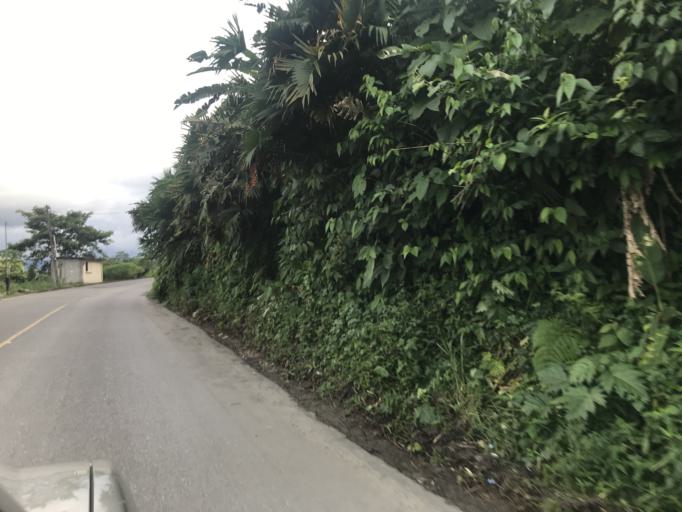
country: EC
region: Napo
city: Tena
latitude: -1.0353
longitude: -77.7544
